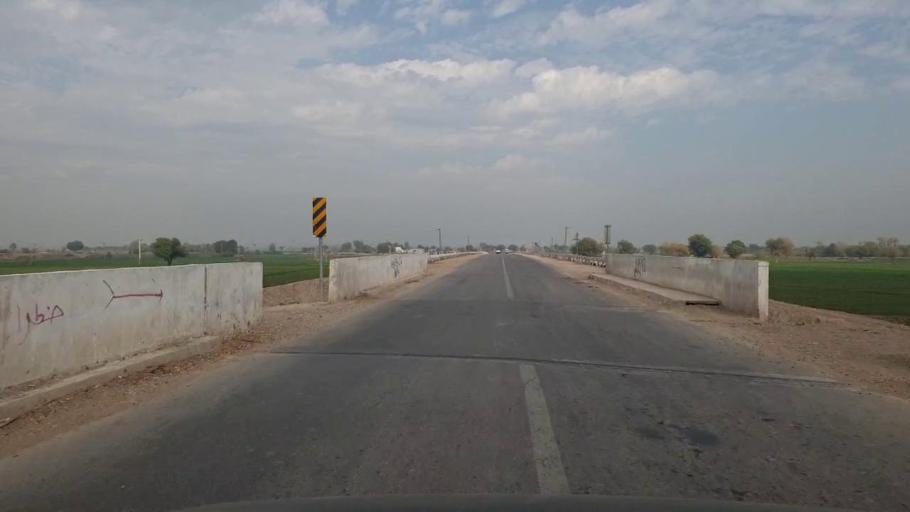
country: PK
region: Sindh
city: Sakrand
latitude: 26.0518
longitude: 68.4101
